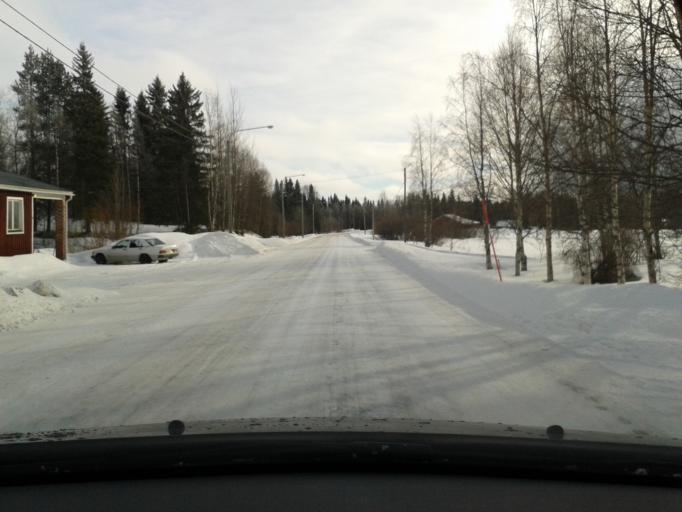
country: SE
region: Vaesterbotten
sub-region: Vilhelmina Kommun
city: Sjoberg
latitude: 64.6853
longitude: 16.2821
